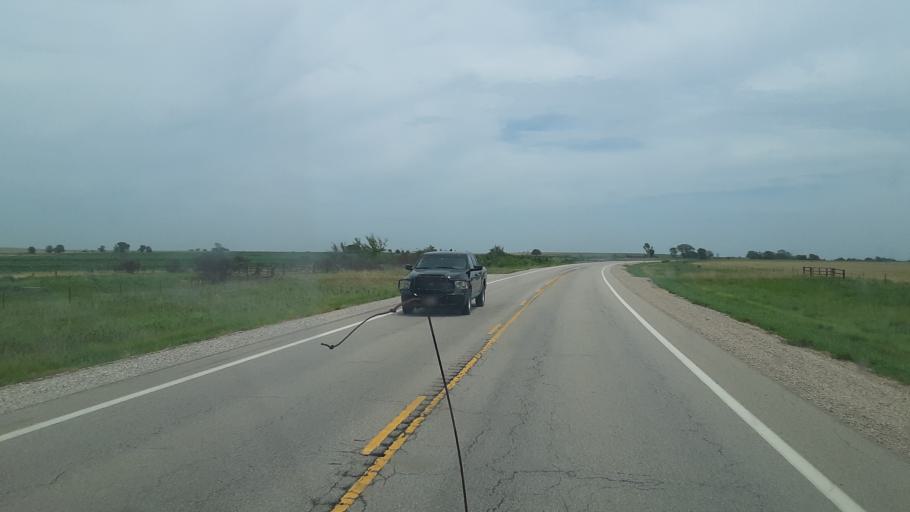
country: US
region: Kansas
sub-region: Woodson County
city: Yates Center
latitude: 37.8660
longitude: -95.8077
